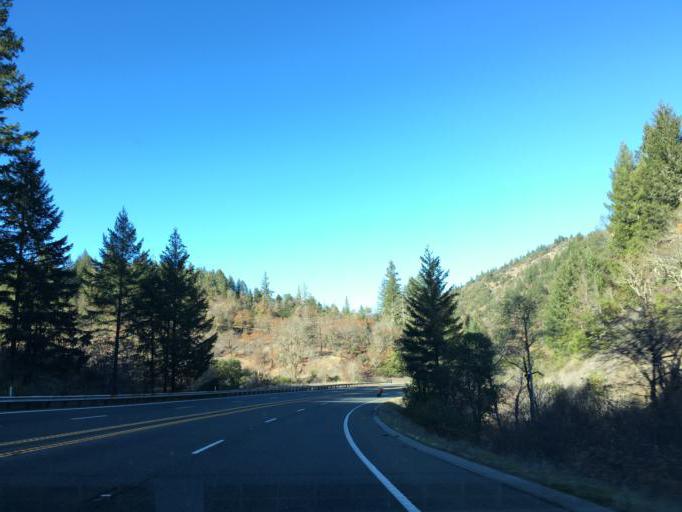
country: US
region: California
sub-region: Mendocino County
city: Laytonville
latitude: 39.5982
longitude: -123.4545
